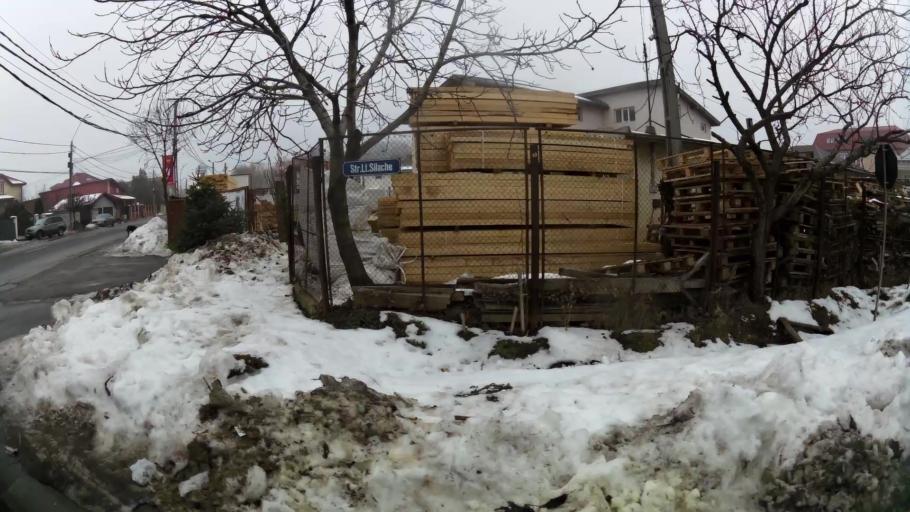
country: RO
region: Ilfov
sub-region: Comuna Chiajna
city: Rosu
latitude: 44.4516
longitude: 26.0020
